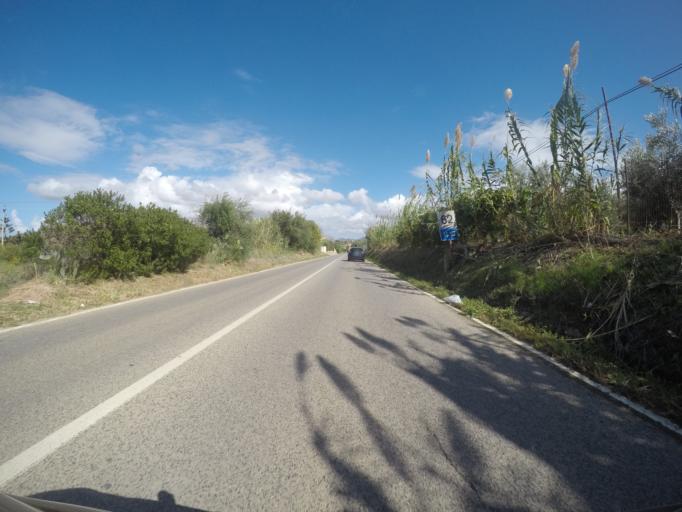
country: IT
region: Sicily
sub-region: Palermo
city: Trappeto
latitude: 38.0720
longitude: 13.0613
